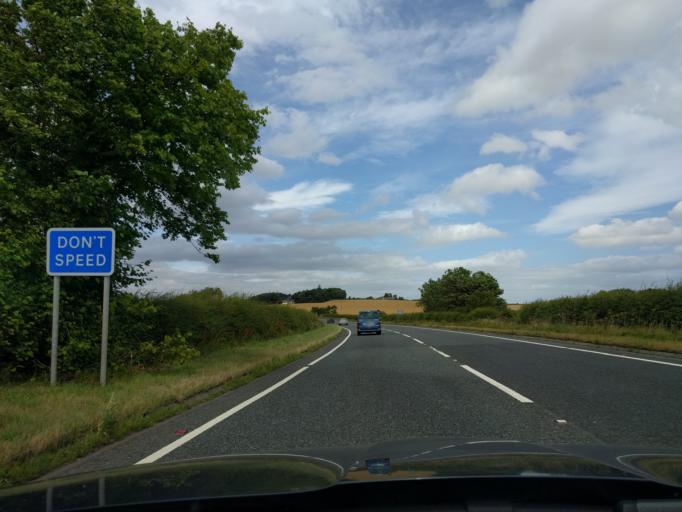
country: GB
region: England
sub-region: Northumberland
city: Felton
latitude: 55.2546
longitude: -1.7023
